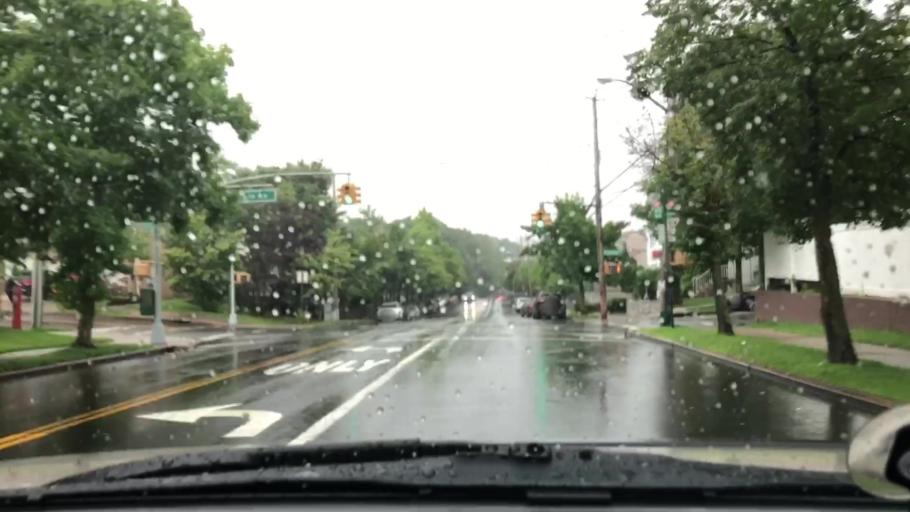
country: US
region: New Jersey
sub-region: Middlesex County
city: Carteret
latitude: 40.5464
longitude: -74.1990
